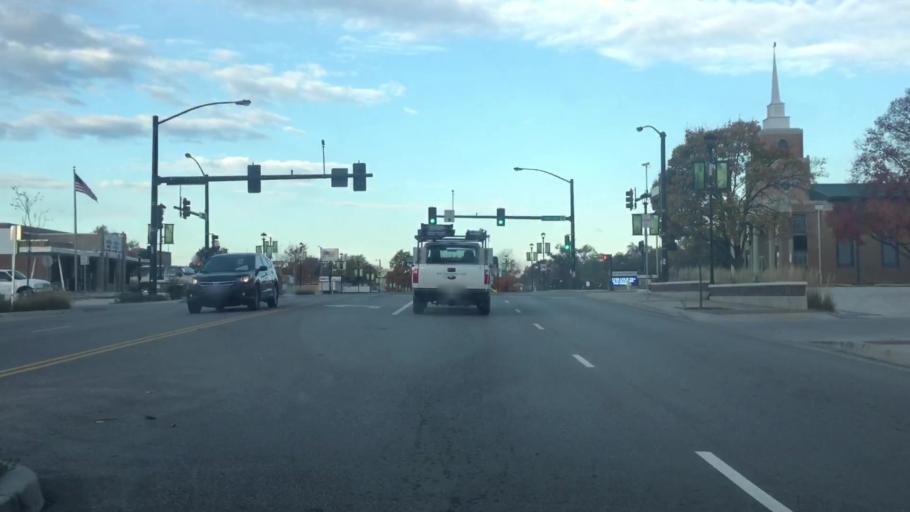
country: US
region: Missouri
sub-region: Jackson County
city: Grandview
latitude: 38.8890
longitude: -94.5274
